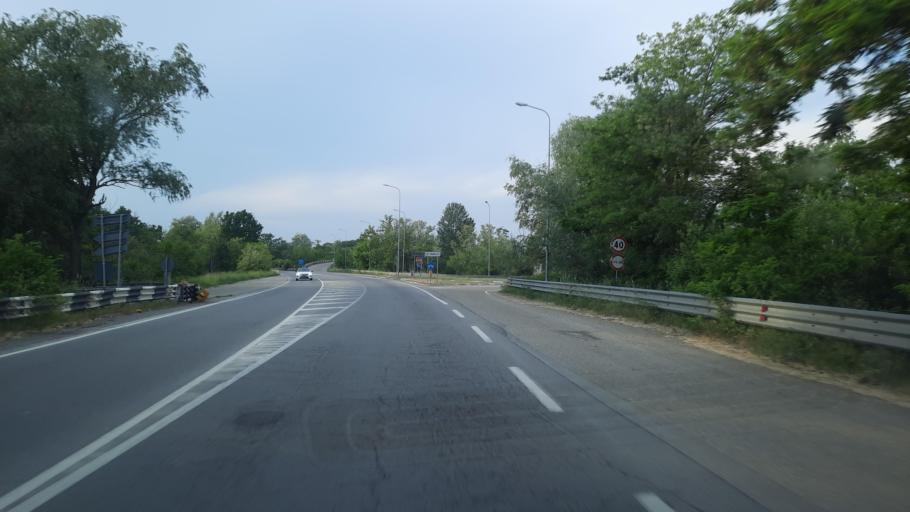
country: IT
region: Lombardy
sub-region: Provincia di Pavia
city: Tromello
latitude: 45.2135
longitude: 8.8586
